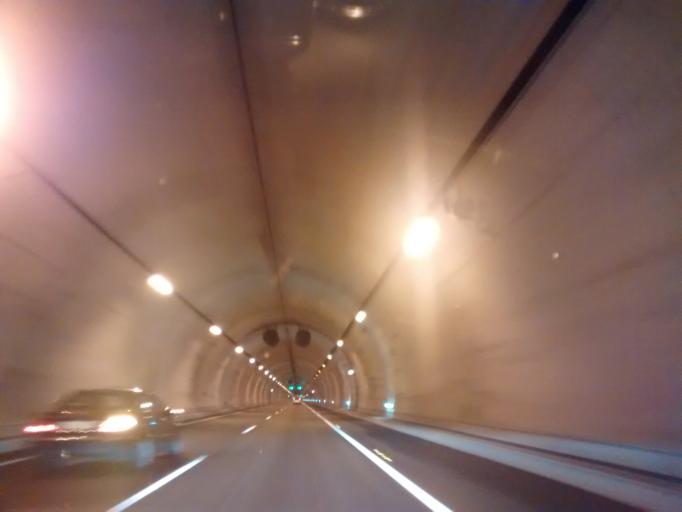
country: ES
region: Cantabria
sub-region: Provincia de Cantabria
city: Los Corrales de Buelna
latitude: 43.2270
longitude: -4.0799
